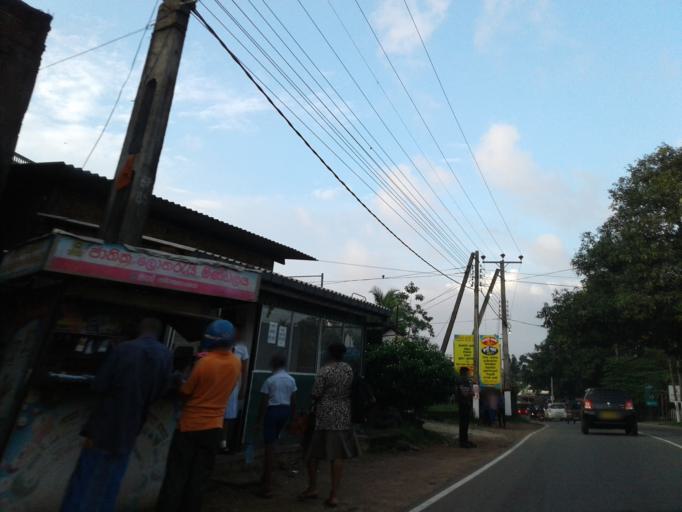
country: LK
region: Western
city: Mulleriyawa
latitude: 6.9695
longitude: 80.0009
